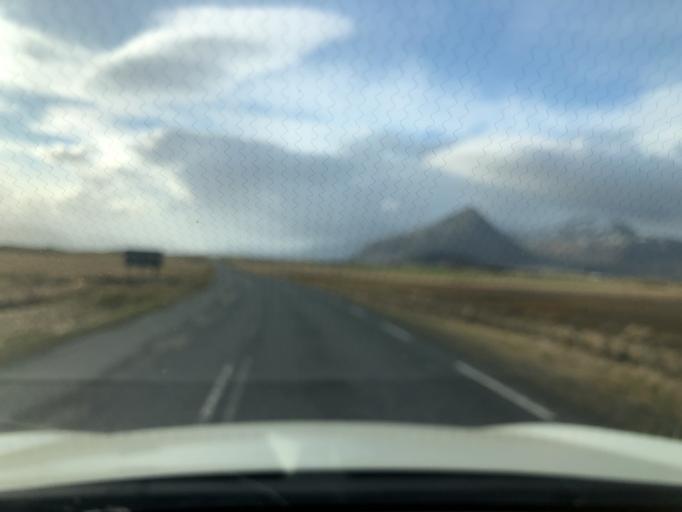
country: IS
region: East
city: Hoefn
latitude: 64.2913
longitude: -15.1835
